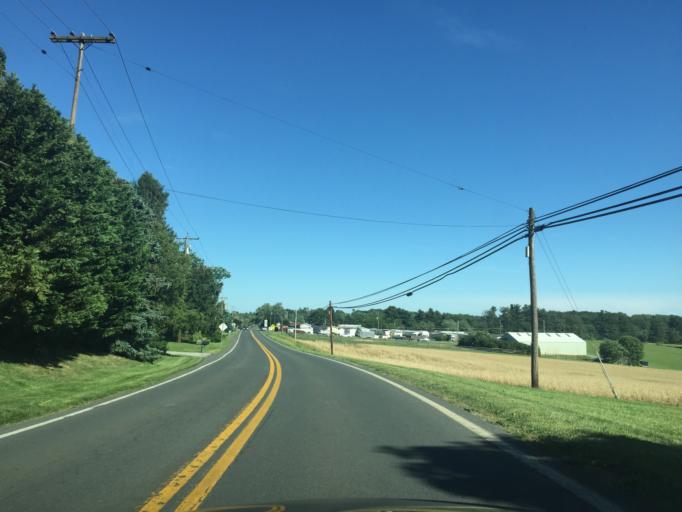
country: US
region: Maryland
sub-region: Carroll County
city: Westminster
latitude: 39.5231
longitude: -76.9233
